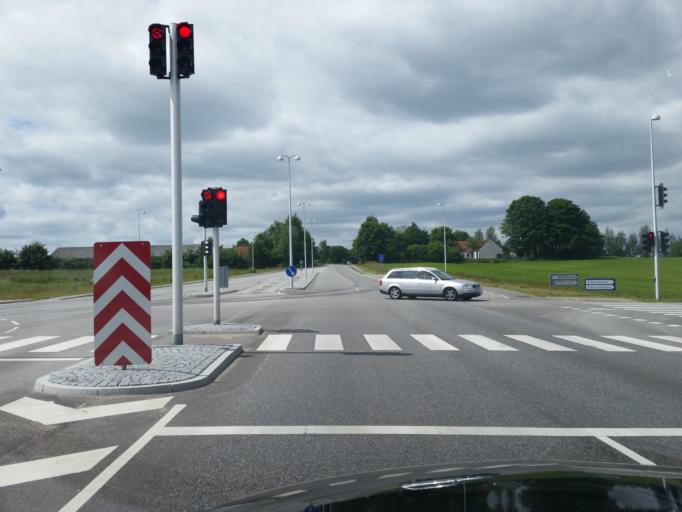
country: DK
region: Central Jutland
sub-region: Horsens Kommune
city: Horsens
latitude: 55.8776
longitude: 9.8096
